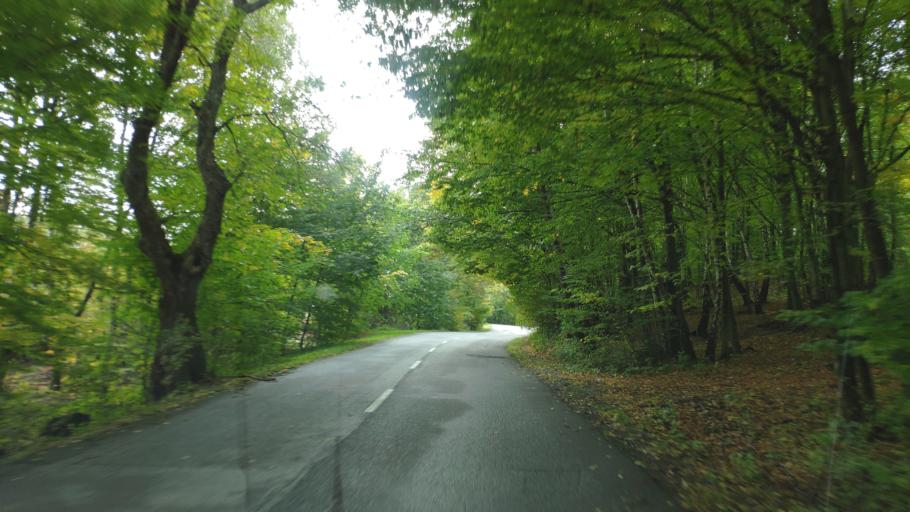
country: SK
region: Presovsky
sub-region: Okres Presov
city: Presov
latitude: 48.9543
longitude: 21.3799
